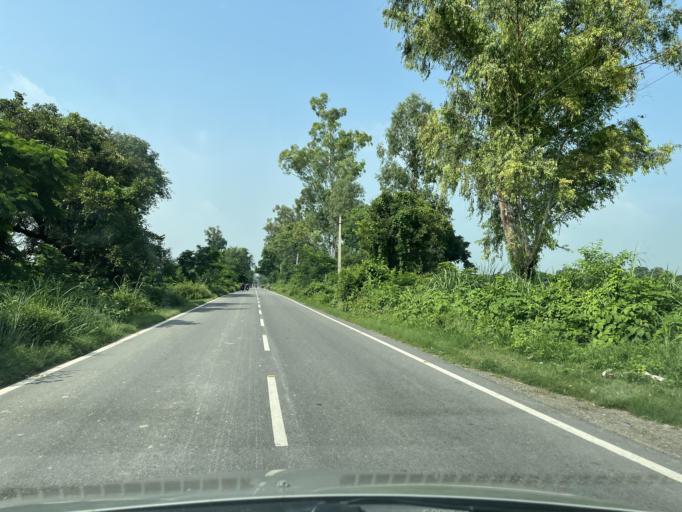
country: IN
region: Uttarakhand
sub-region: Udham Singh Nagar
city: Bazpur
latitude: 29.1860
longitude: 79.1851
